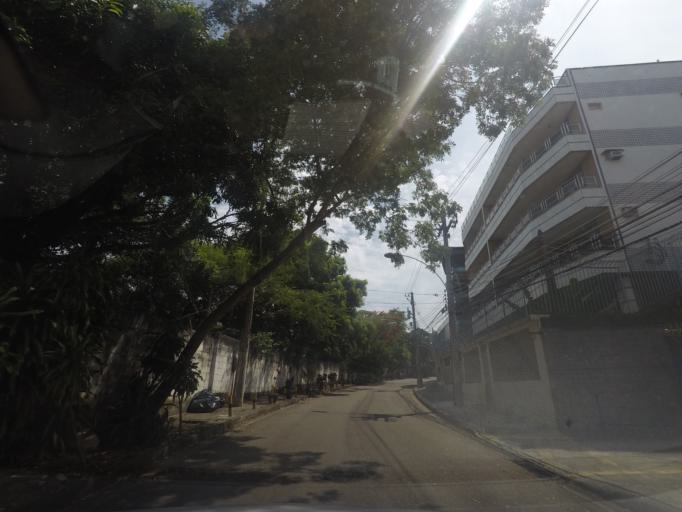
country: BR
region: Rio de Janeiro
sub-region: Rio De Janeiro
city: Rio de Janeiro
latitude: -22.8142
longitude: -43.2077
